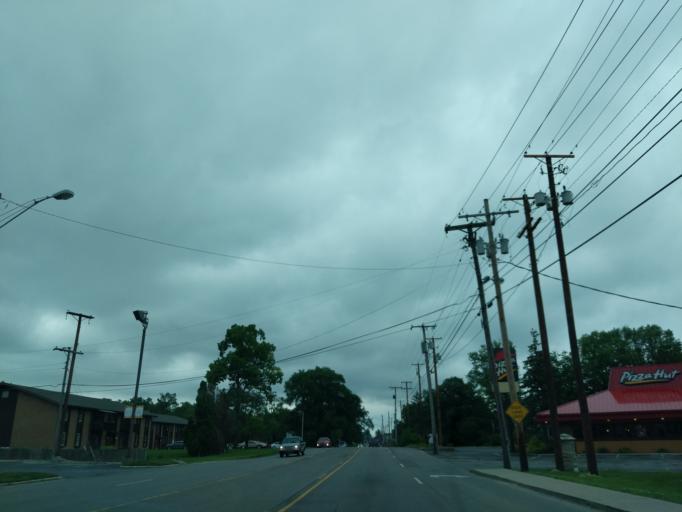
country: US
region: Indiana
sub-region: Delaware County
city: Muncie
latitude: 40.2151
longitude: -85.4005
